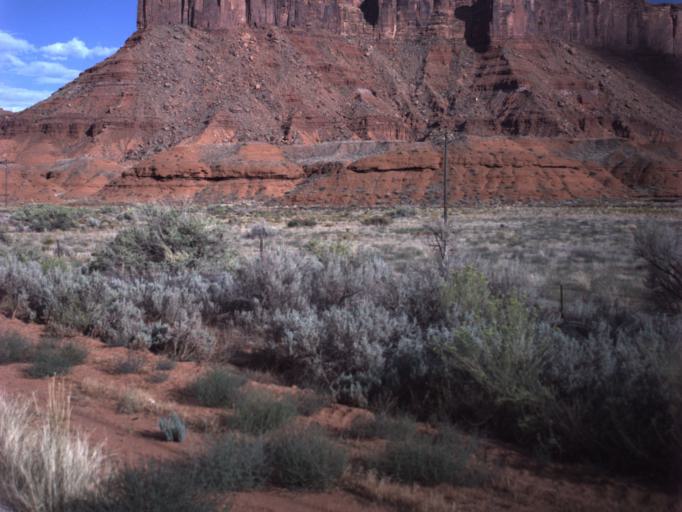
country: US
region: Utah
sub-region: Grand County
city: Moab
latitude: 38.6828
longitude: -109.4254
